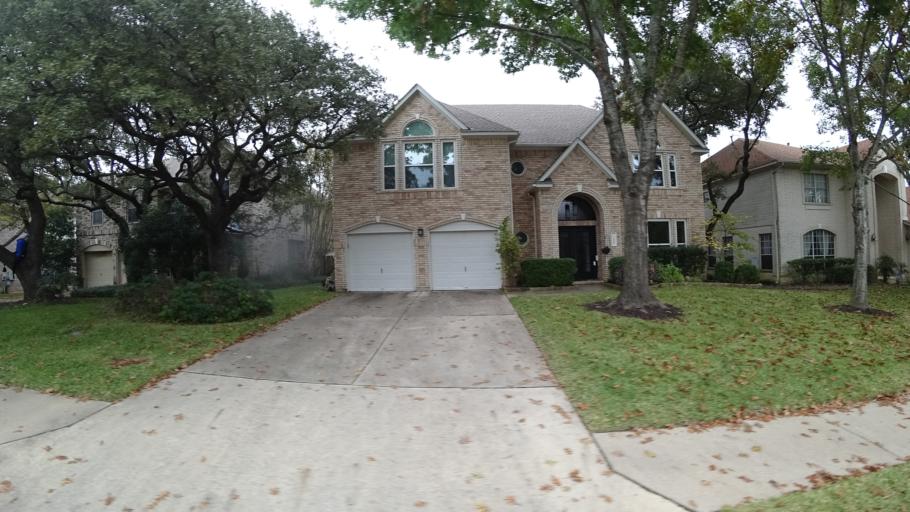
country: US
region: Texas
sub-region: Williamson County
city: Anderson Mill
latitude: 30.4351
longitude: -97.8217
